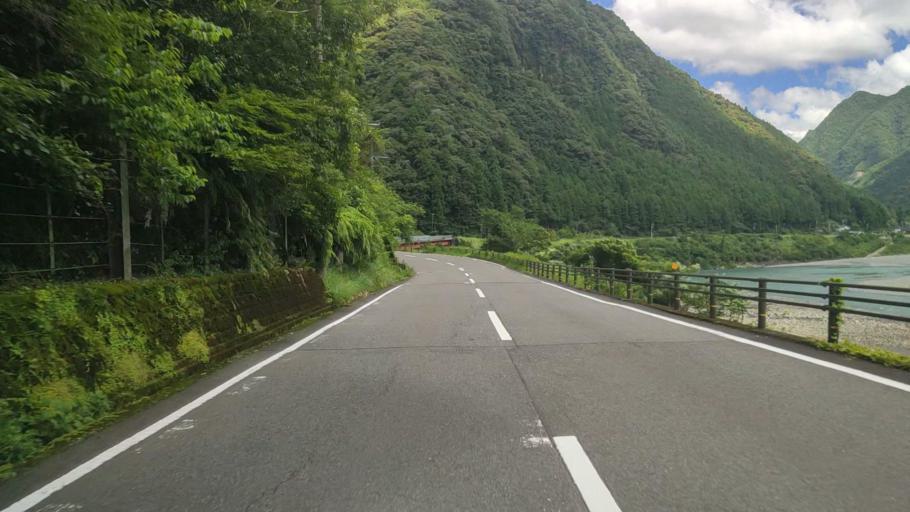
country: JP
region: Wakayama
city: Shingu
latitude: 33.7842
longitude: 135.8972
